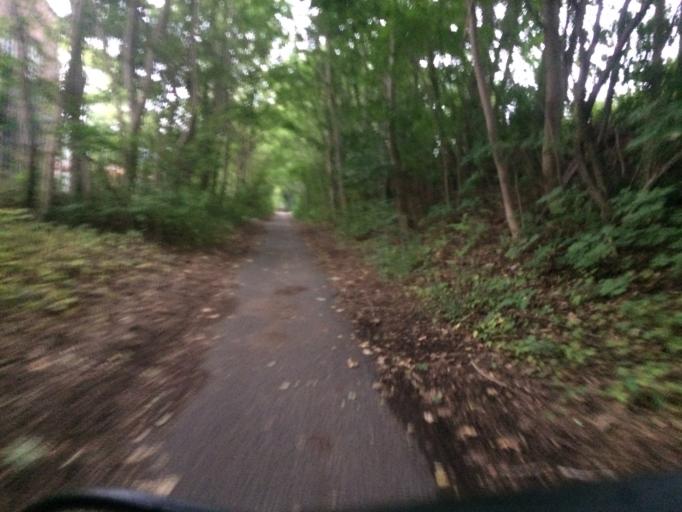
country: DE
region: Berlin
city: Markisches Viertel
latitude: 52.5860
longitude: 13.3549
